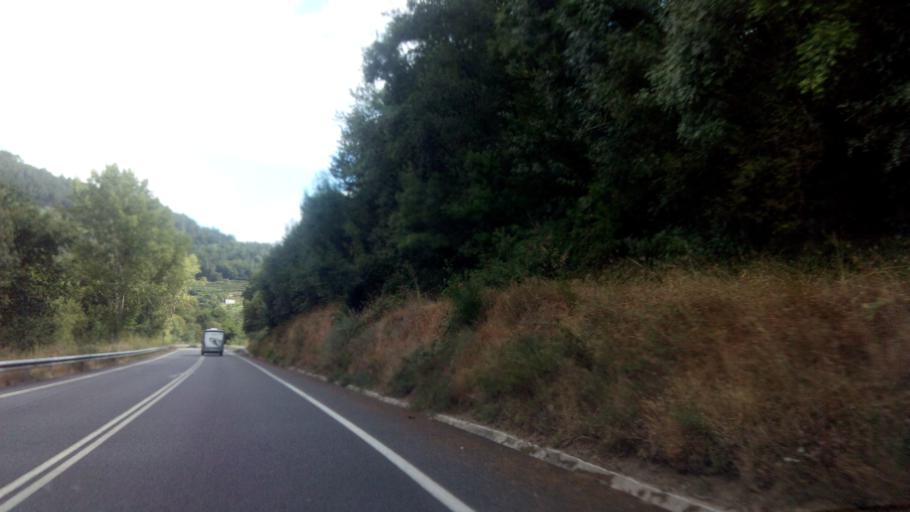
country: ES
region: Galicia
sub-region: Provincia de Ourense
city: Nogueira de Ramuin
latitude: 42.4155
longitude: -7.7787
